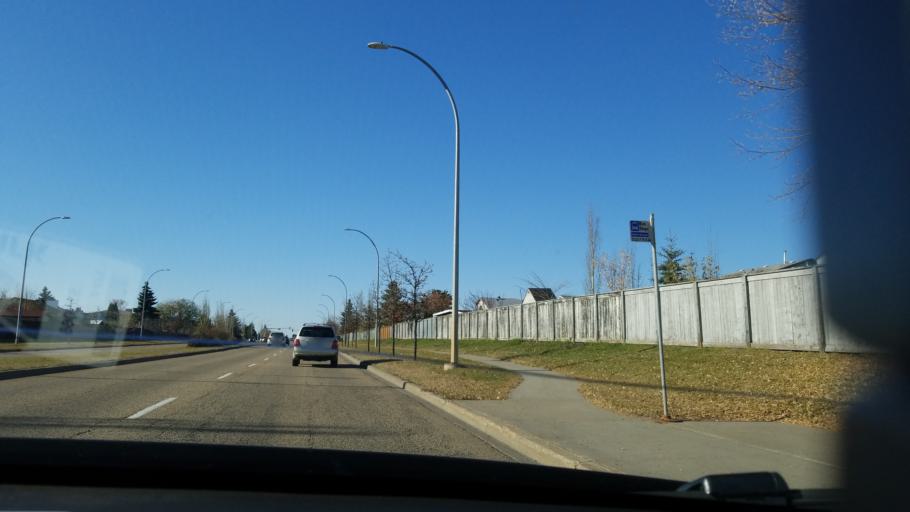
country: CA
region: Alberta
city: Edmonton
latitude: 53.6159
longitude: -113.4611
